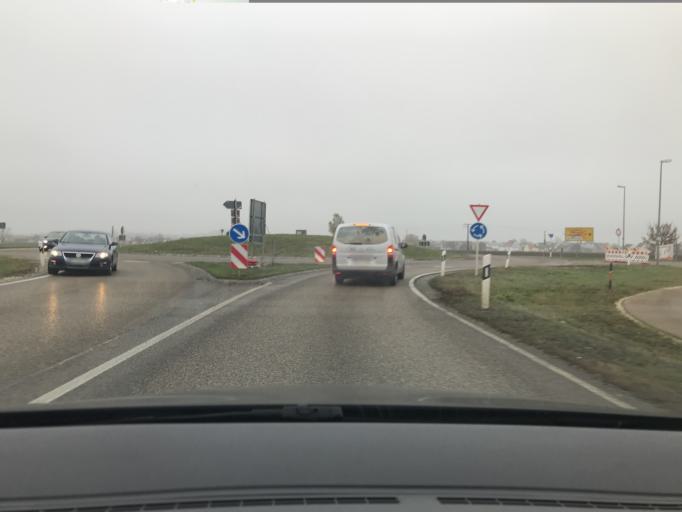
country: DE
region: Bavaria
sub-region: Swabia
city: Wallerstein
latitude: 48.8689
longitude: 10.4731
